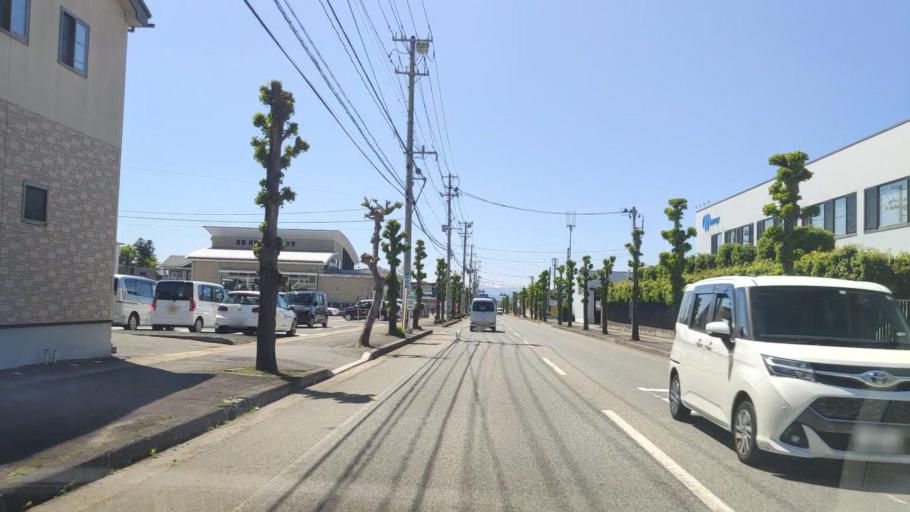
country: JP
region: Yamagata
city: Tendo
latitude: 38.3733
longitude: 140.3776
